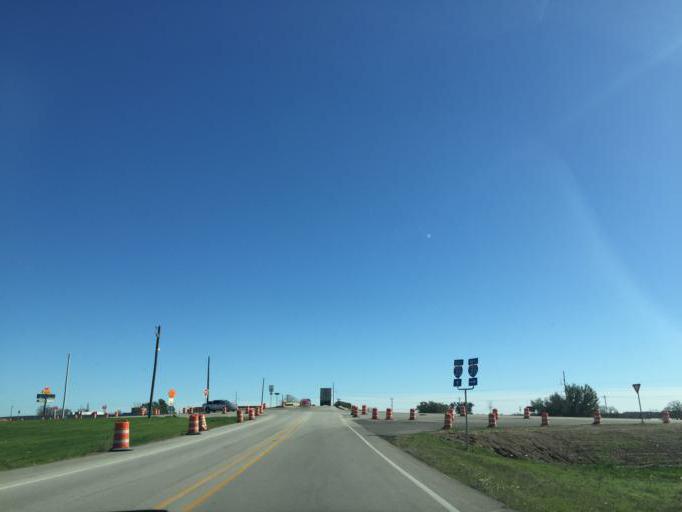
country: US
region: Texas
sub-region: Parker County
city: Hudson Oaks
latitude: 32.7440
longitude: -97.7477
